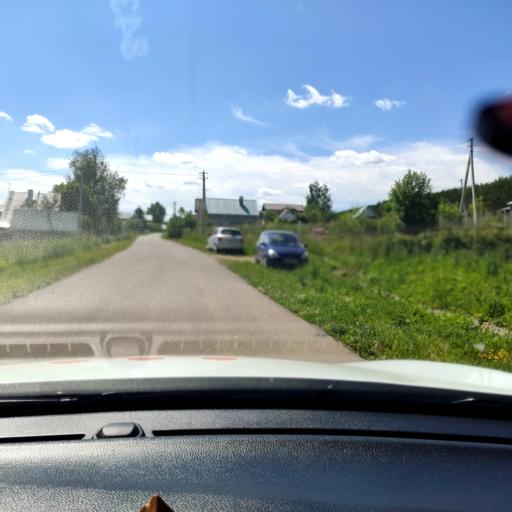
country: RU
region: Tatarstan
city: Sviyazhsk
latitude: 55.7716
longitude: 48.7697
